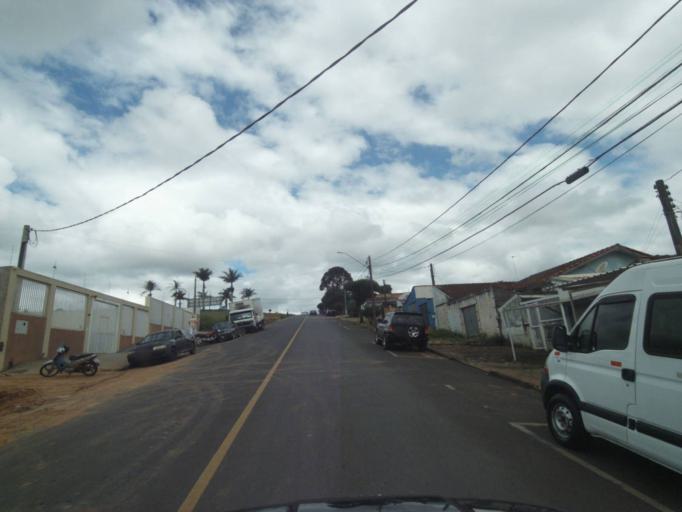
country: BR
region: Parana
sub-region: Telemaco Borba
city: Telemaco Borba
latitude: -24.3171
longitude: -50.6429
